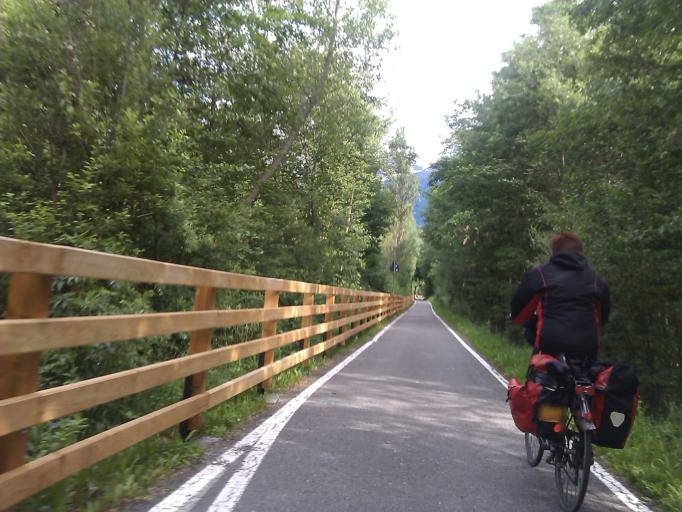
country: IT
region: Trentino-Alto Adige
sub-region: Bolzano
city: Sluderno
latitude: 46.6521
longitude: 10.5728
